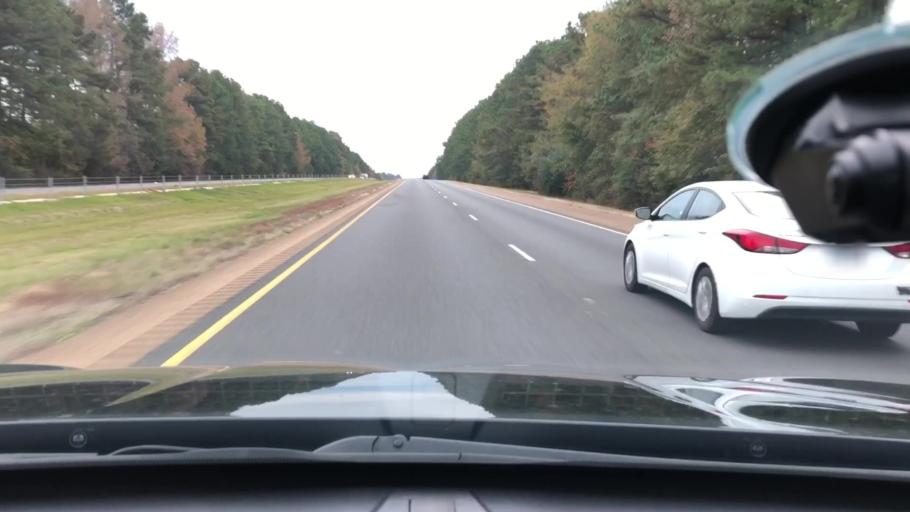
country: US
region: Arkansas
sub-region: Clark County
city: Gurdon
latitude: 33.9741
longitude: -93.2063
